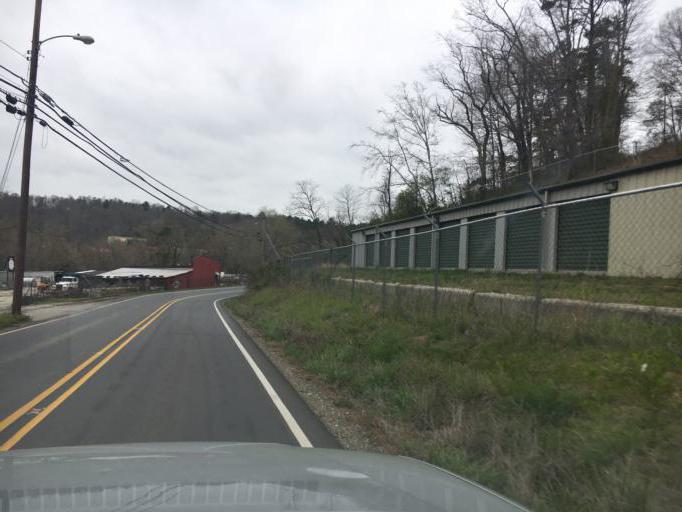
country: US
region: North Carolina
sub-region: Buncombe County
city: Woodfin
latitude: 35.6262
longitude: -82.6000
